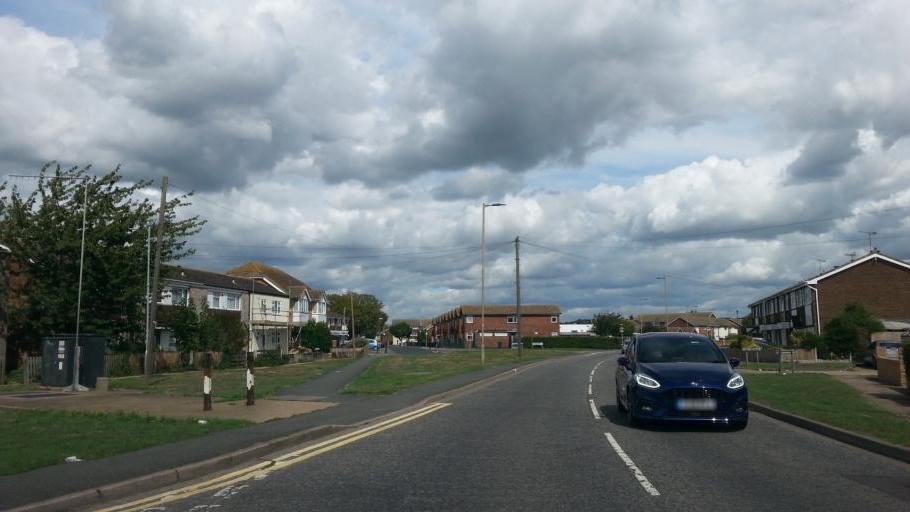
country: GB
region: England
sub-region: Essex
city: Canvey Island
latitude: 51.5231
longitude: 0.5677
